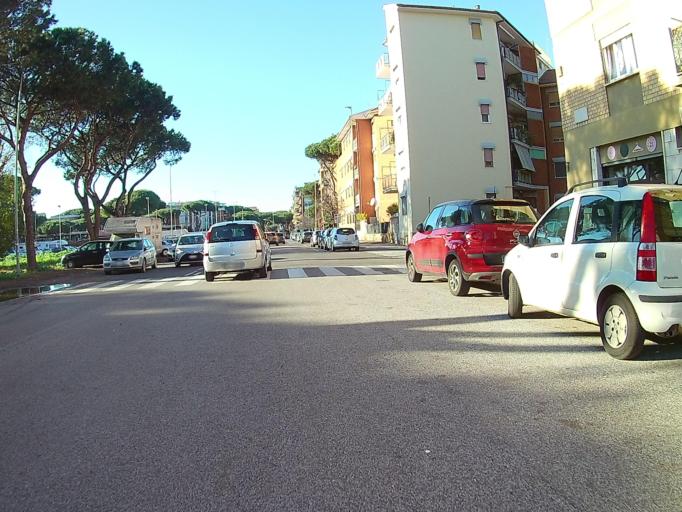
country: IT
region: Latium
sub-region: Citta metropolitana di Roma Capitale
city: Lido di Ostia
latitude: 41.7355
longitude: 12.2940
